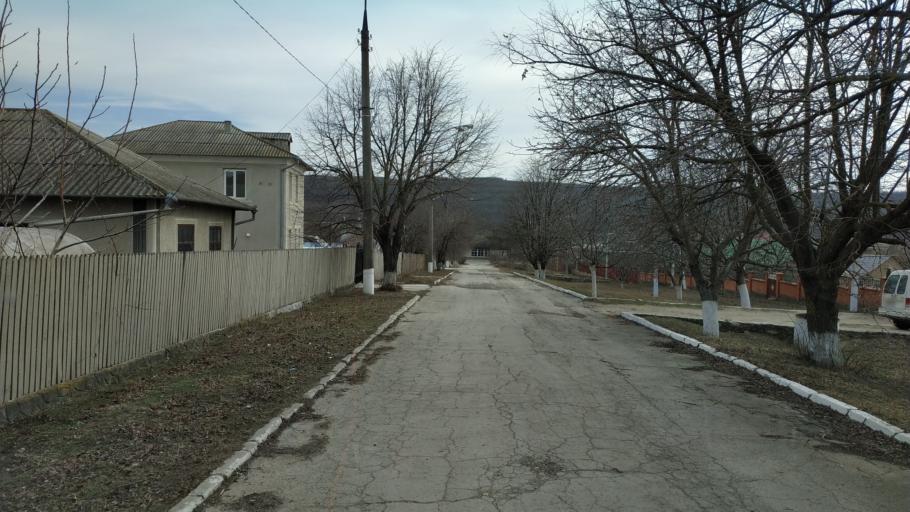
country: MD
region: Hincesti
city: Dancu
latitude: 46.8607
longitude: 28.2489
